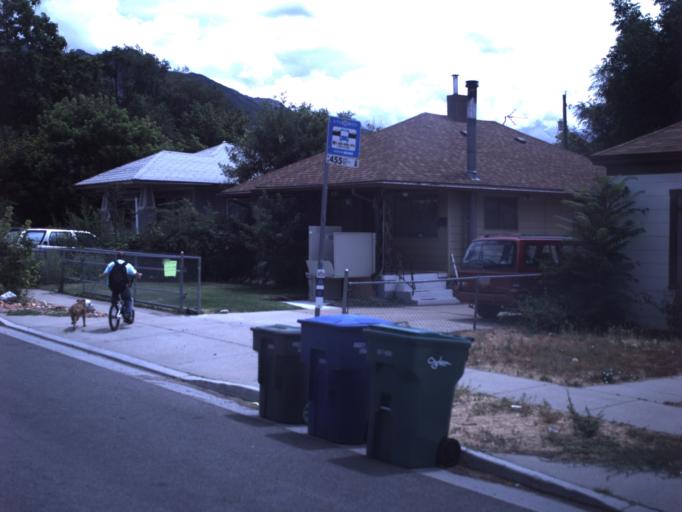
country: US
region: Utah
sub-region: Weber County
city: Ogden
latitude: 41.2101
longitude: -111.9649
